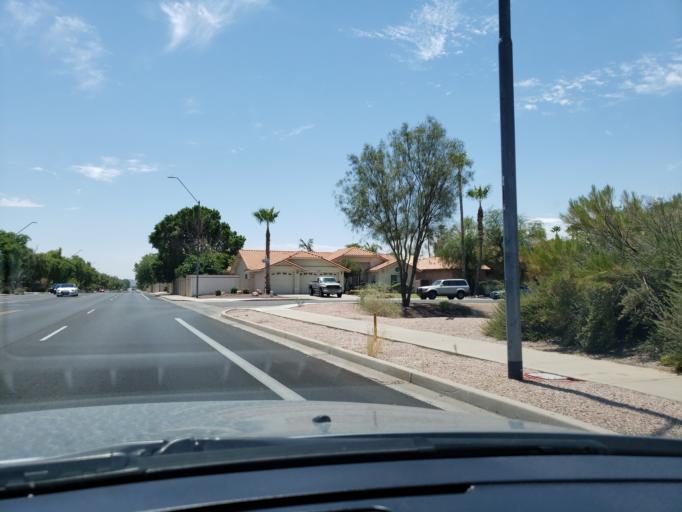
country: US
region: Arizona
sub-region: Maricopa County
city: Paradise Valley
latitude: 33.6226
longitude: -111.9431
